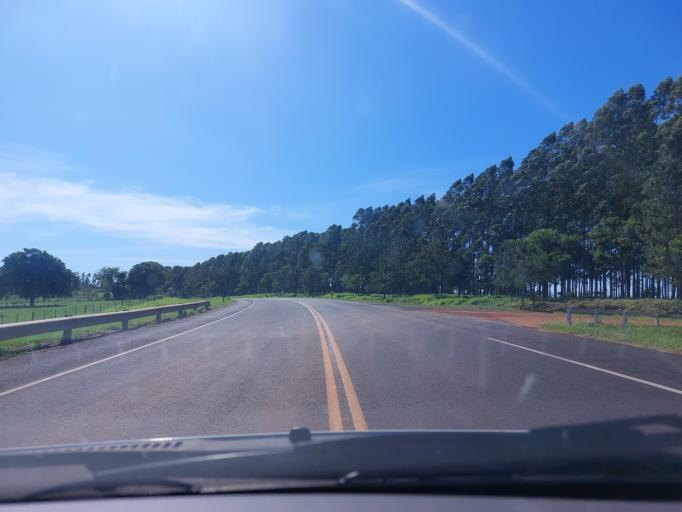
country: PY
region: San Pedro
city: Itacurubi del Rosario
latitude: -24.6034
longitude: -56.7621
